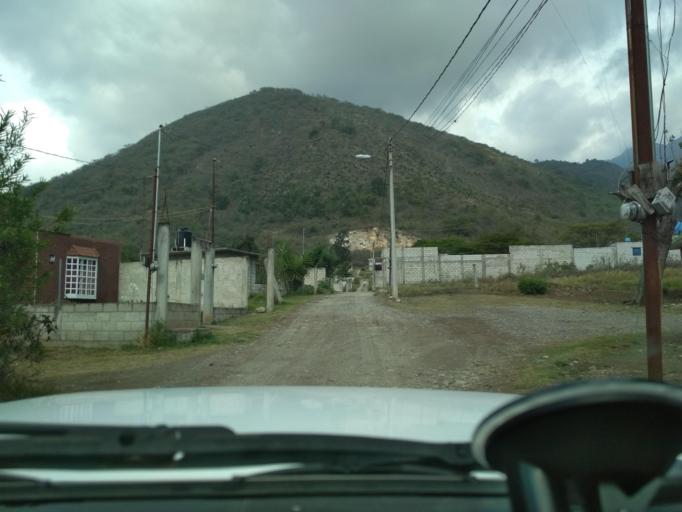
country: MX
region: Veracruz
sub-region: Nogales
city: Taza de Agua Ojo Zarco
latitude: 18.7852
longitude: -97.1986
